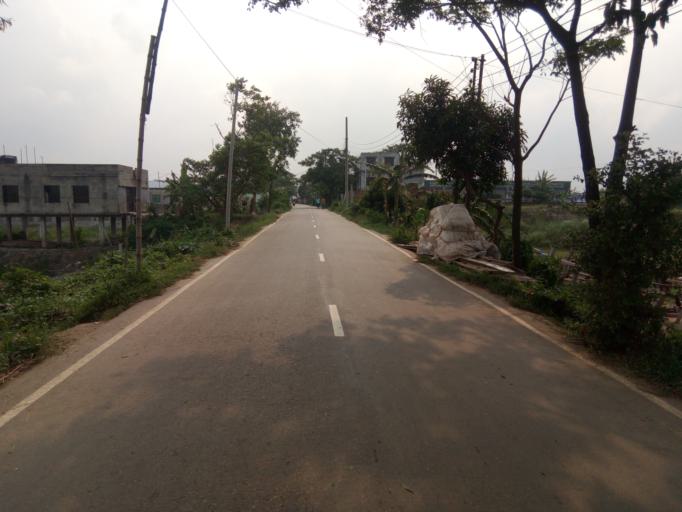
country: BD
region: Dhaka
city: Paltan
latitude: 23.7454
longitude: 90.4655
